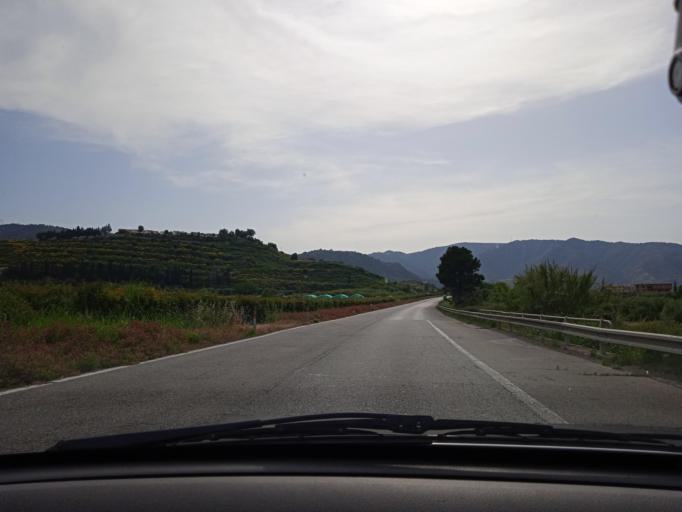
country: IT
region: Sicily
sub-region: Messina
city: Falcone
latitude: 38.1135
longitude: 15.0936
